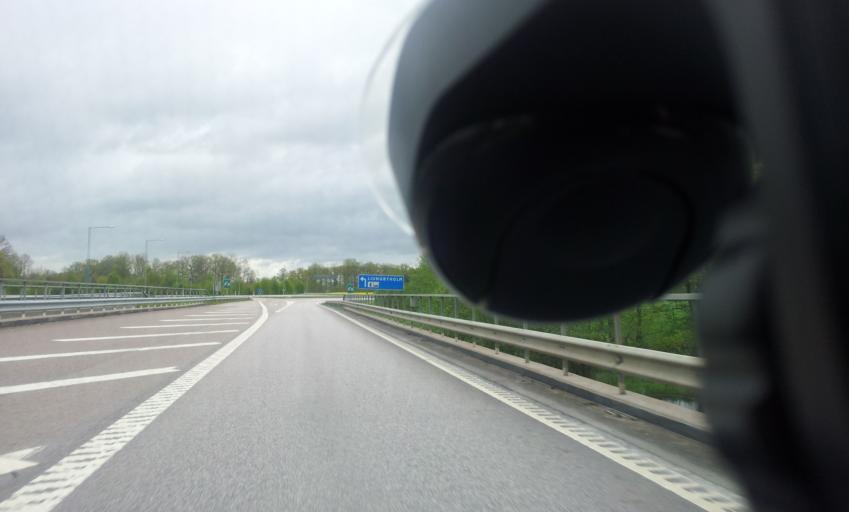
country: SE
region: Kalmar
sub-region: Kalmar Kommun
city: Ljungbyholm
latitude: 56.6361
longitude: 16.2119
